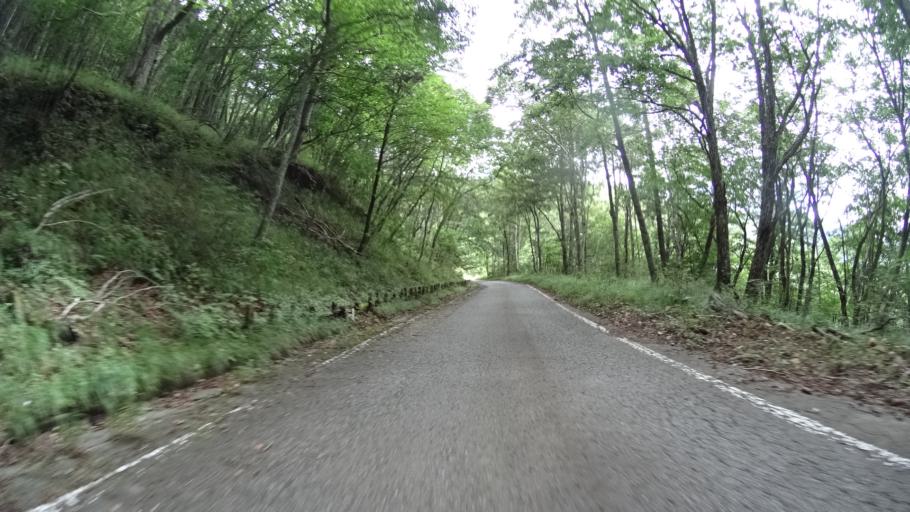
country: JP
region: Yamanashi
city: Kofu-shi
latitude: 35.8160
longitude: 138.5554
